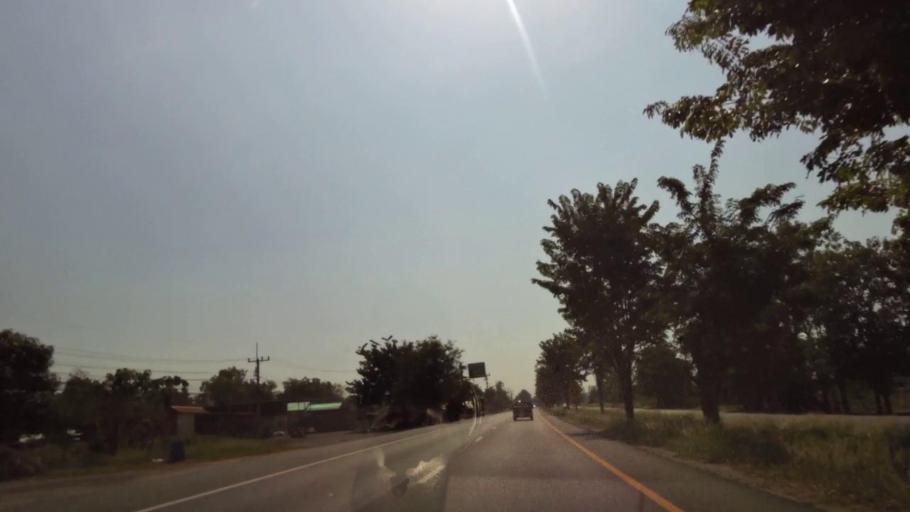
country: TH
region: Nakhon Sawan
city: Kao Liao
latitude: 15.9597
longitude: 100.1187
